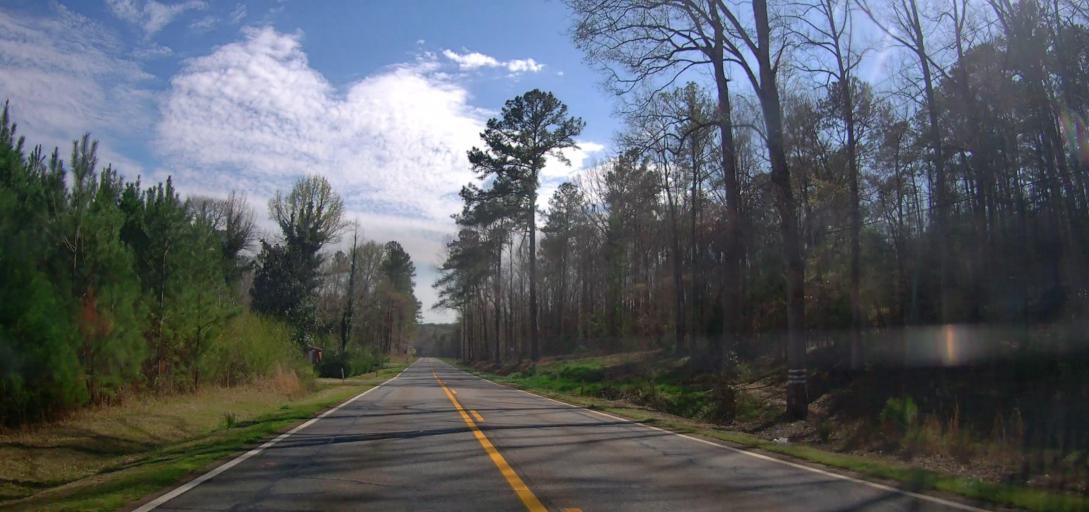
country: US
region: Georgia
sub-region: Monroe County
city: Forsyth
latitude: 33.1290
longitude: -83.9439
